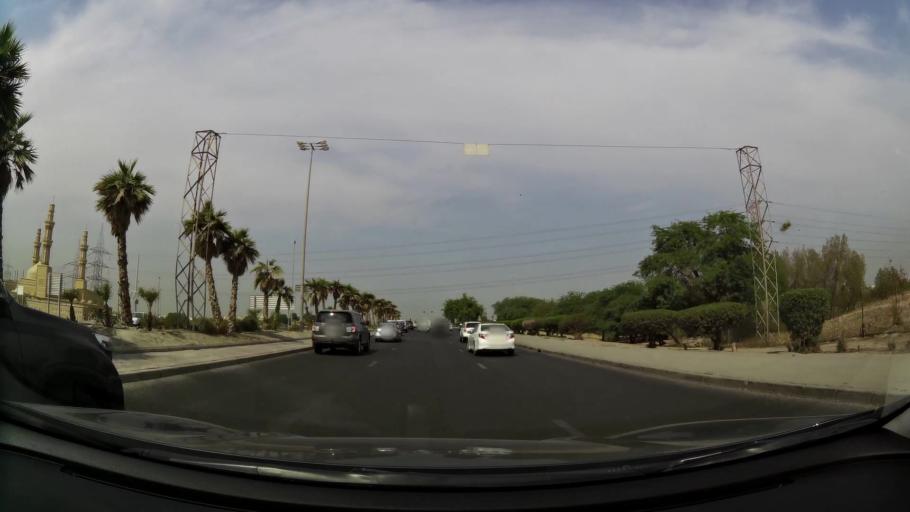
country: KW
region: Muhafazat Hawalli
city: Hawalli
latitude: 29.3031
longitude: 48.0007
